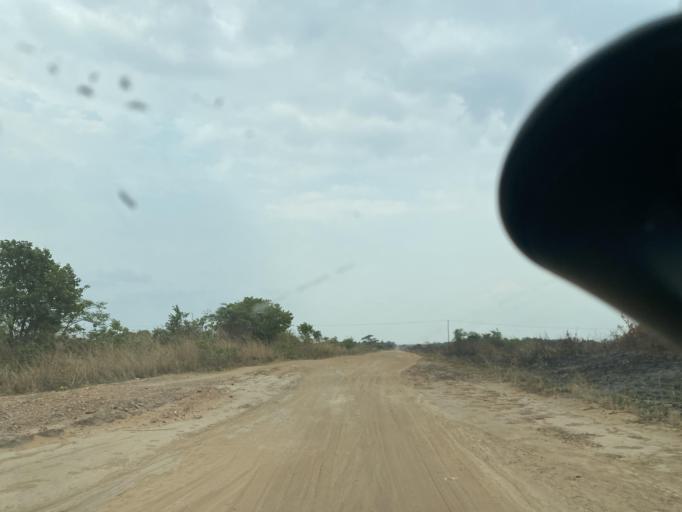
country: ZM
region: Lusaka
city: Lusaka
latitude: -15.2133
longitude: 28.3389
